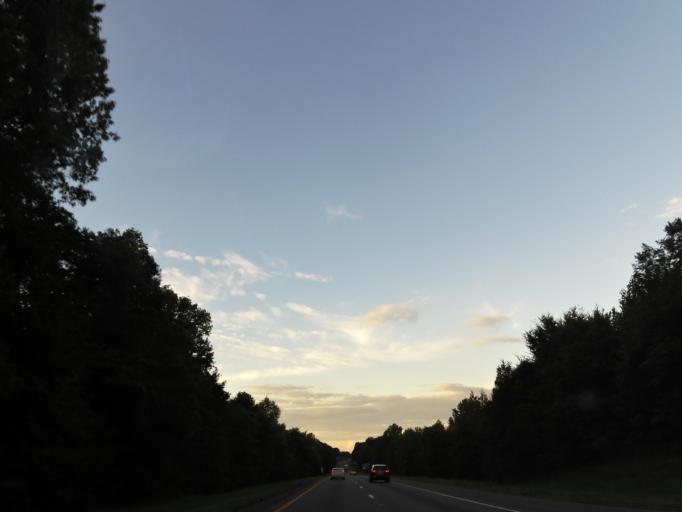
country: US
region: Tennessee
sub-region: McMinn County
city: Athens
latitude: 35.4425
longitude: -84.6726
